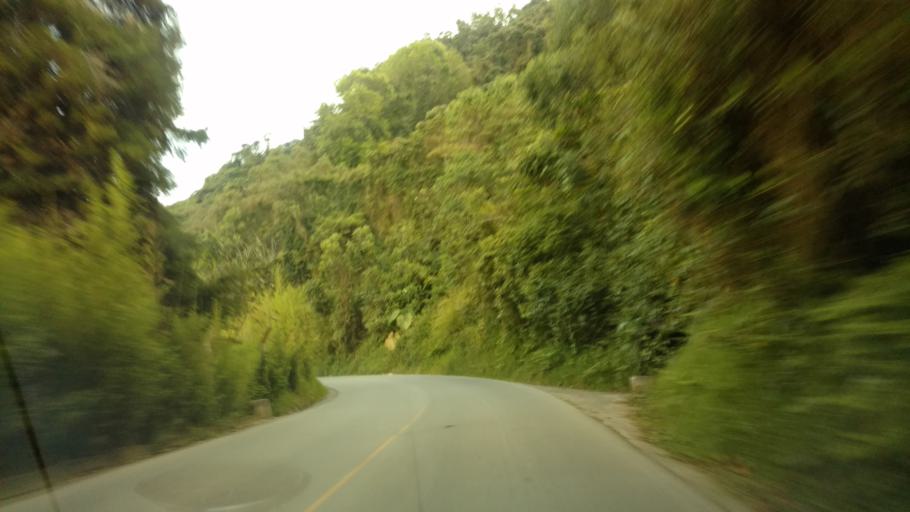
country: CO
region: Caldas
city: Aranzazu
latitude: 5.2890
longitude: -75.4885
